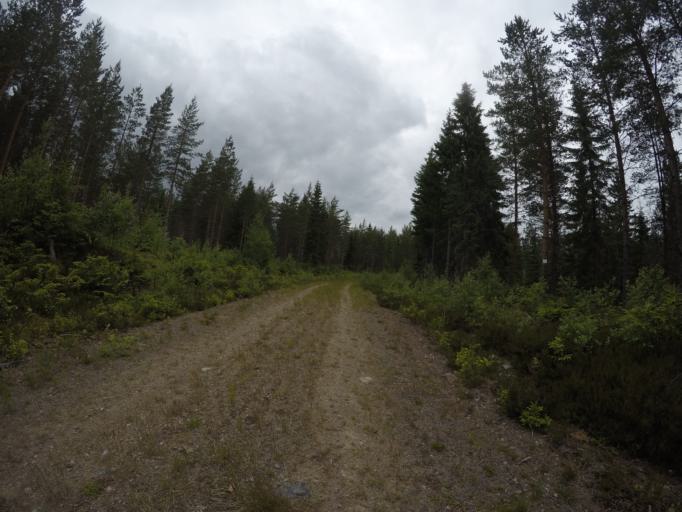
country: SE
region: Dalarna
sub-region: Ludvika Kommun
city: Abborrberget
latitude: 60.0793
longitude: 14.5199
